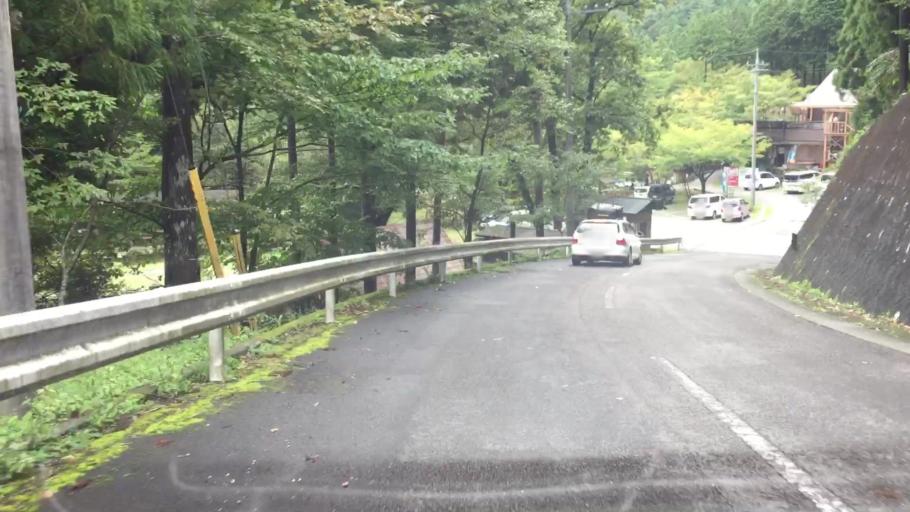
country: JP
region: Tochigi
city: Imaichi
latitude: 36.7603
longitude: 139.6673
